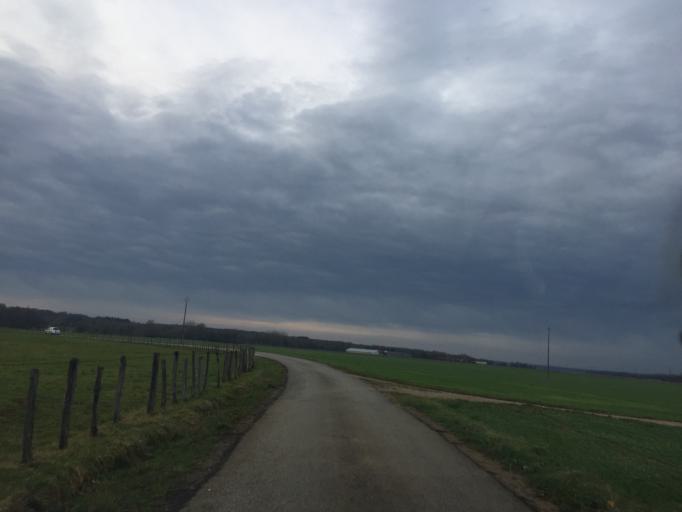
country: FR
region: Franche-Comte
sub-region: Departement du Jura
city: Mont-sous-Vaudrey
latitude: 46.9453
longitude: 5.6656
